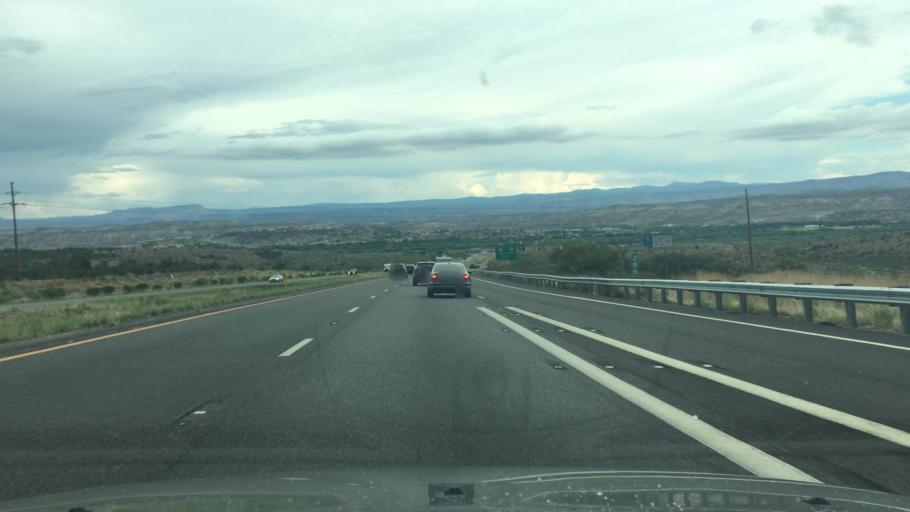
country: US
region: Arizona
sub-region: Yavapai County
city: Camp Verde
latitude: 34.5659
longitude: -111.8995
